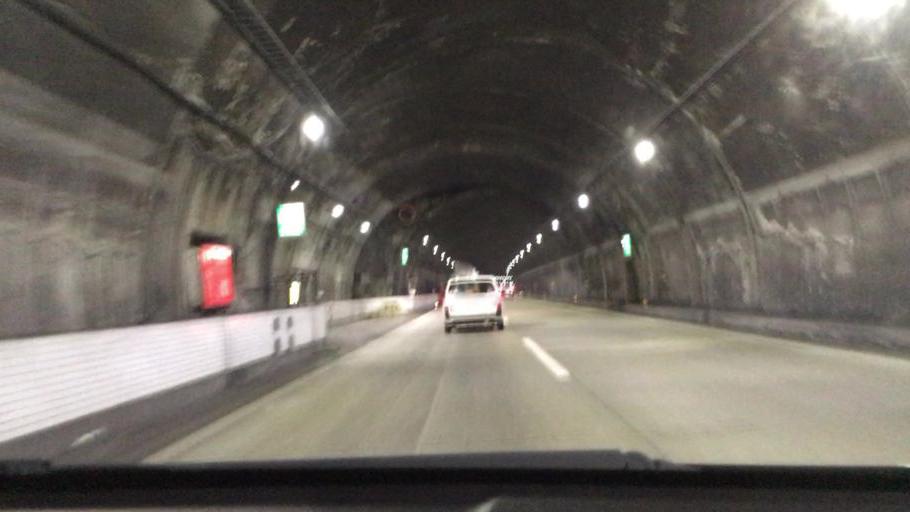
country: JP
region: Yamaguchi
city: Tokuyama
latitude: 34.0716
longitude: 131.7102
